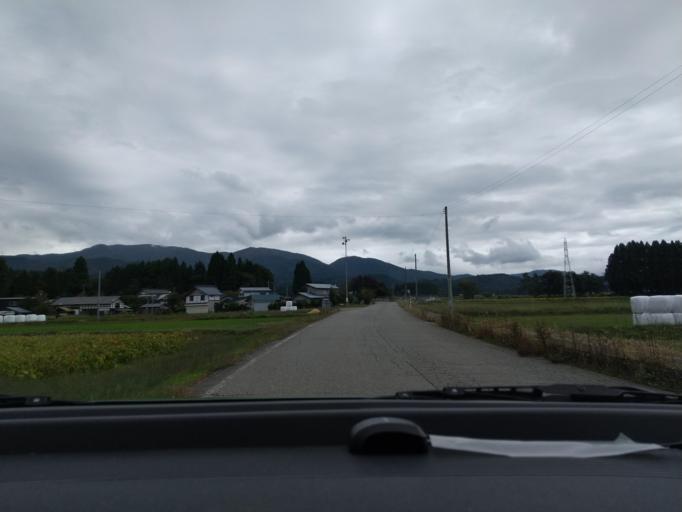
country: JP
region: Akita
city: Kakunodatemachi
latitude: 39.5898
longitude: 140.5999
